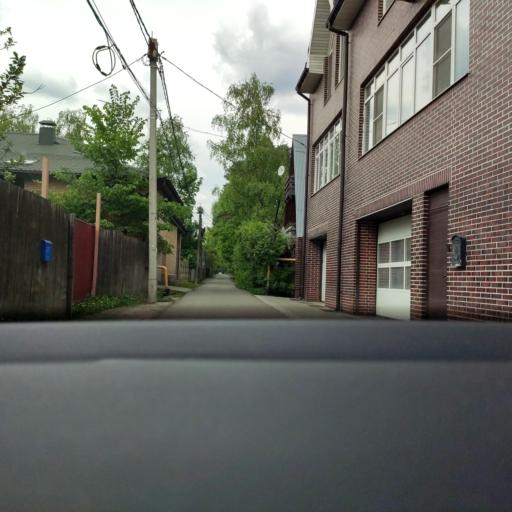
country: RU
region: Moscow
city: Vagonoremont
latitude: 55.9054
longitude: 37.5586
